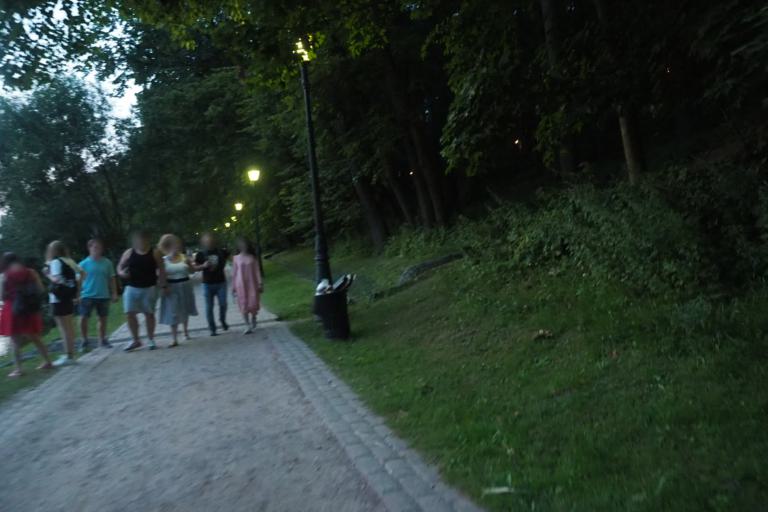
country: RU
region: Moscow
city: Orekhovo-Borisovo Severnoye
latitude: 55.6108
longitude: 37.6811
